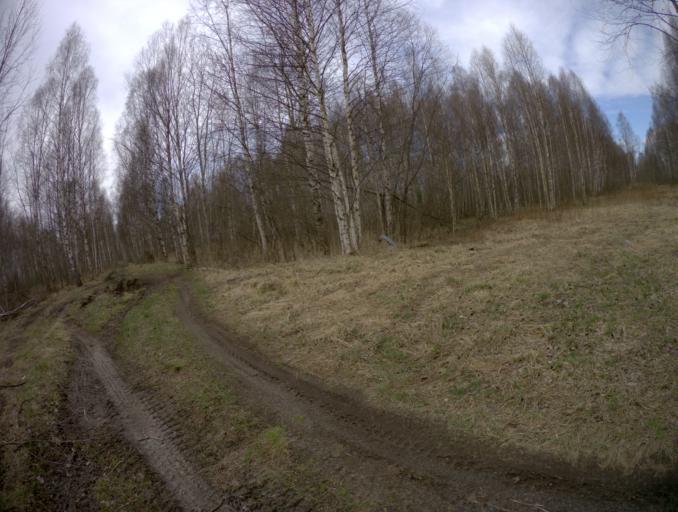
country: RU
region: Vladimir
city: Raduzhnyy
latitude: 55.9126
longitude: 40.2450
